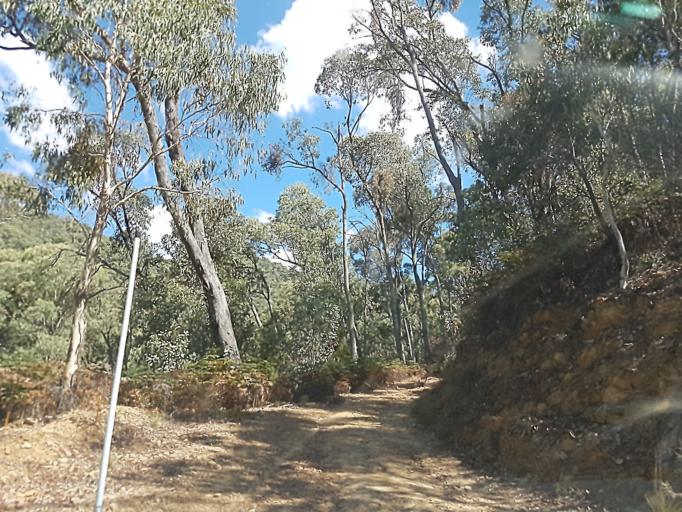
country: AU
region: Victoria
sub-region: Alpine
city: Mount Beauty
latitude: -36.8791
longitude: 147.0417
